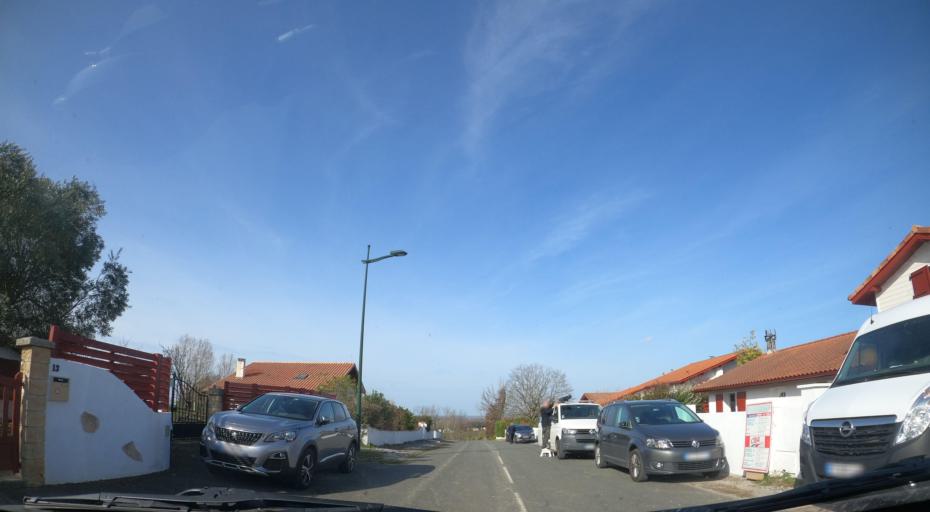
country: FR
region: Aquitaine
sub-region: Departement des Pyrenees-Atlantiques
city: Briscous
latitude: 43.4294
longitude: -1.3757
